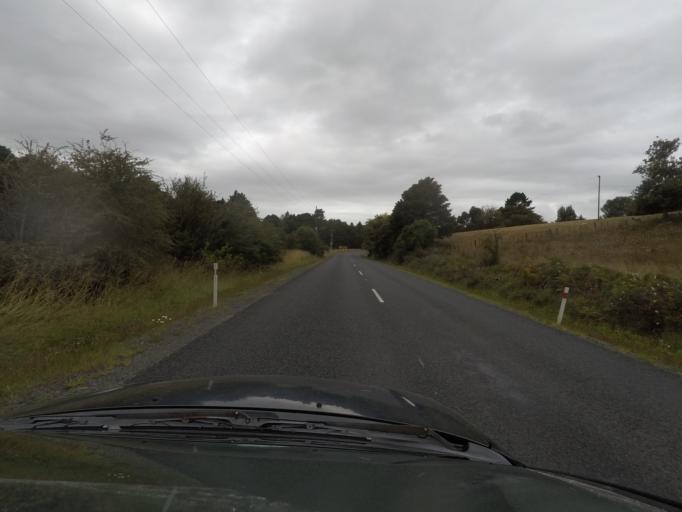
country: NZ
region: Auckland
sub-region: Auckland
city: Wellsford
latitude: -36.2795
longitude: 174.5807
